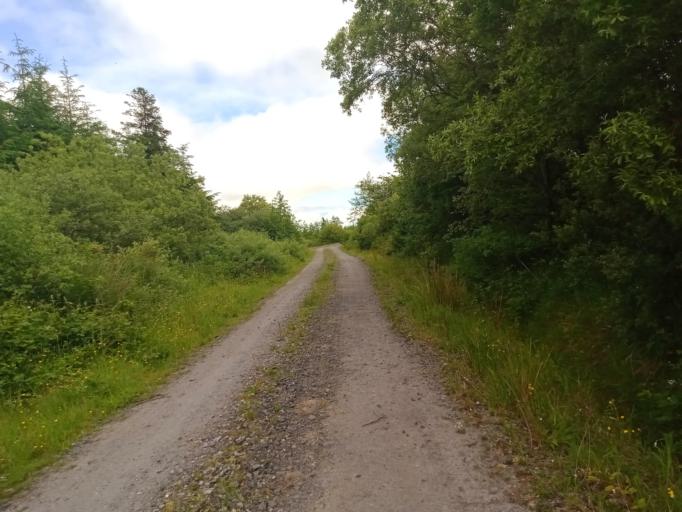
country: IE
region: Leinster
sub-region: Kilkenny
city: Ballyragget
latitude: 52.7906
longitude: -7.4456
